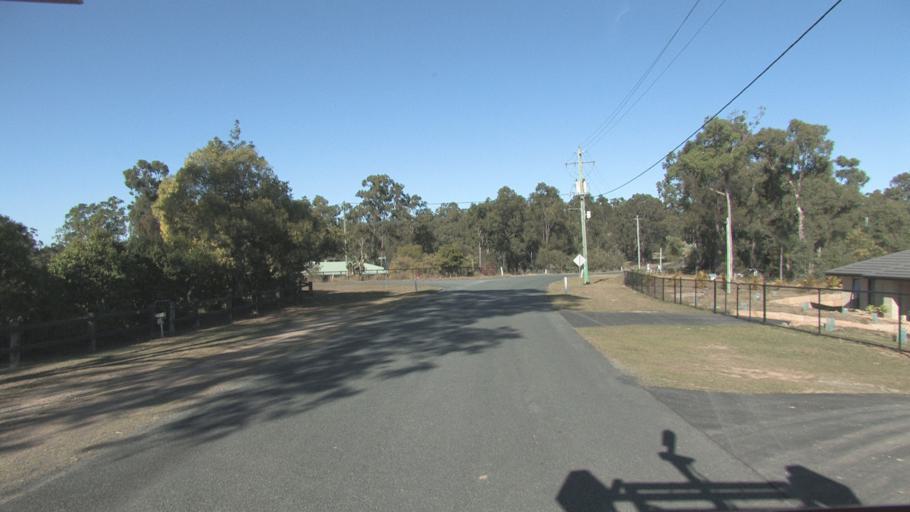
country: AU
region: Queensland
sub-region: Ipswich
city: Springfield Lakes
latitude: -27.6966
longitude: 152.9320
